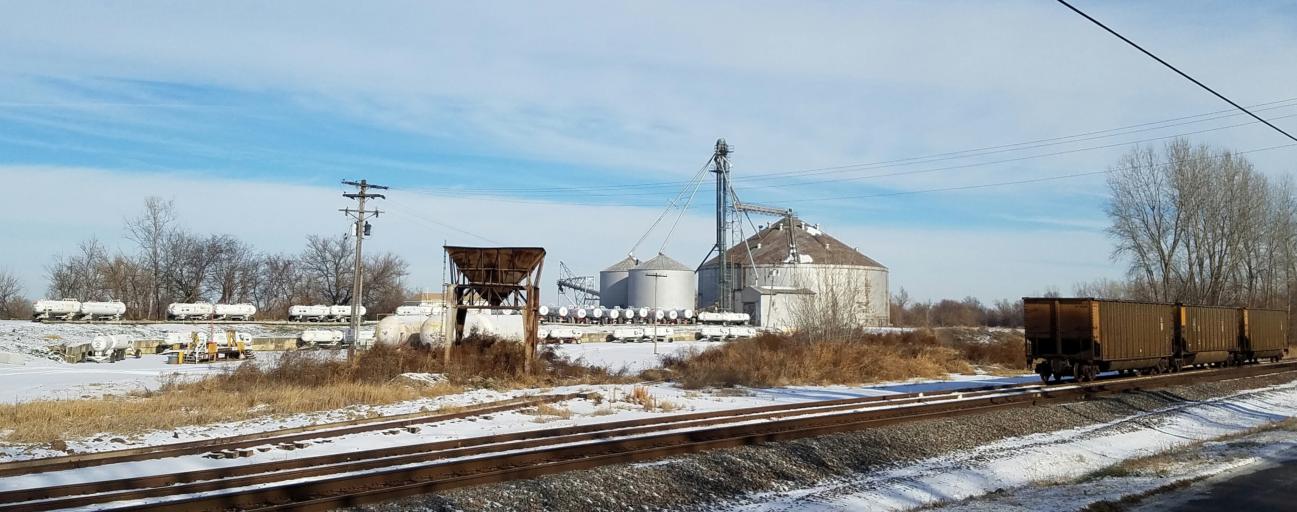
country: US
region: Missouri
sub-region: Lafayette County
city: Lexington
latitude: 39.1734
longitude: -93.9067
